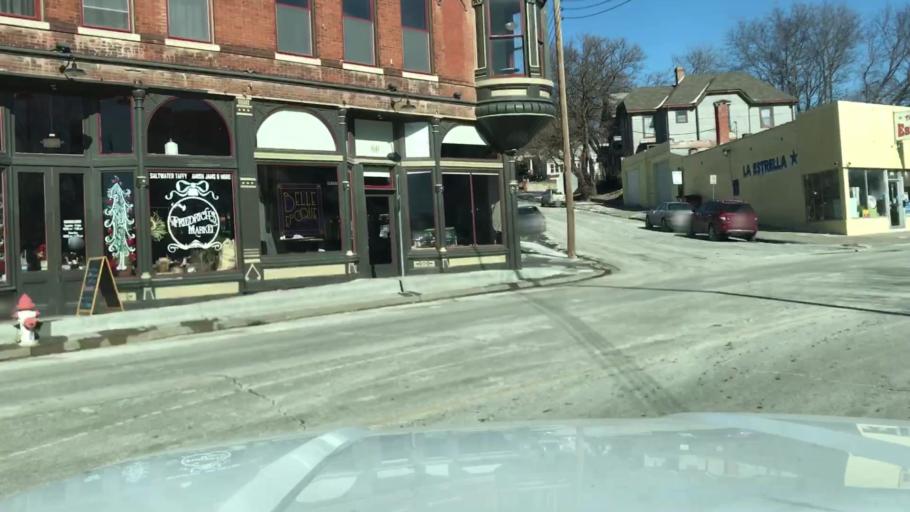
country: US
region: Missouri
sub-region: Buchanan County
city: Saint Joseph
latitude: 39.7698
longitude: -94.8454
